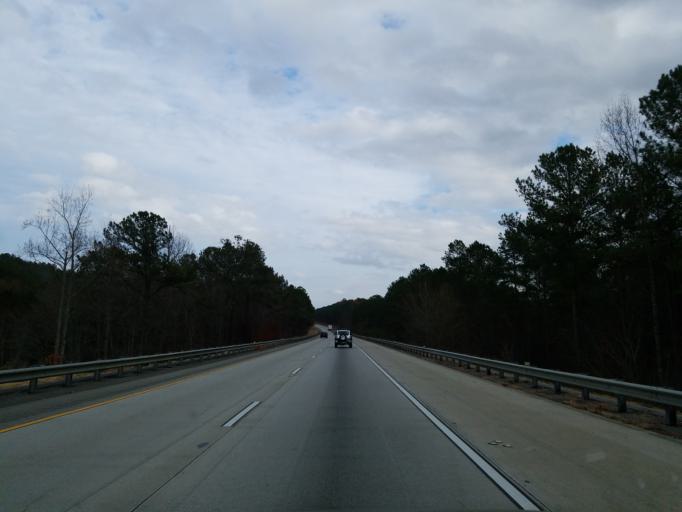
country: US
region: Georgia
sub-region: Carroll County
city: Mount Zion
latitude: 33.6872
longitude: -85.2304
